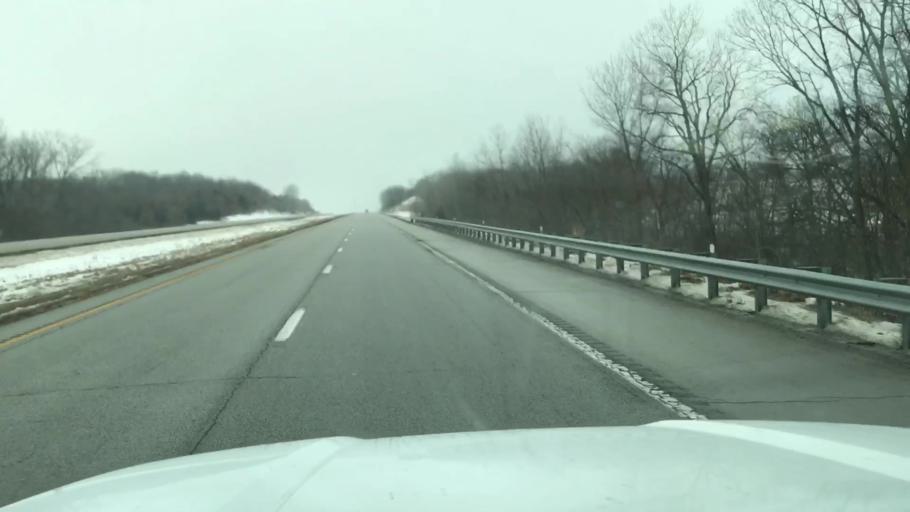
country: US
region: Missouri
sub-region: Clinton County
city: Gower
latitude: 39.7567
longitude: -94.5807
